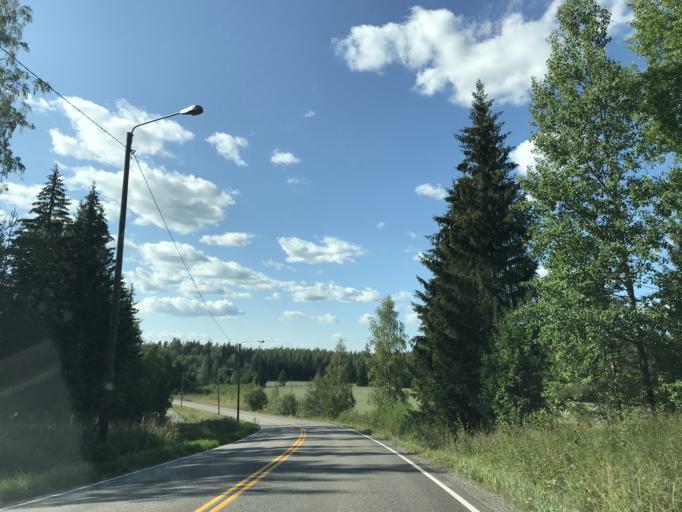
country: FI
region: Uusimaa
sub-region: Helsinki
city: Nurmijaervi
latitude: 60.4081
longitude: 24.8996
